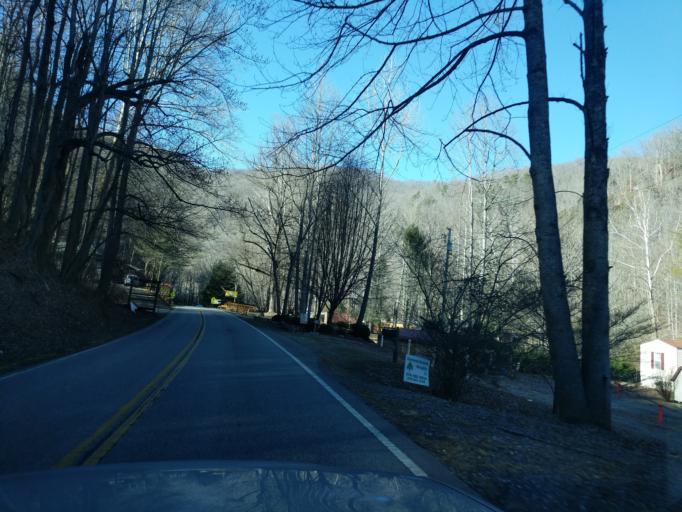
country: US
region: North Carolina
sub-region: Swain County
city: Bryson City
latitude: 35.3340
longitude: -83.6133
